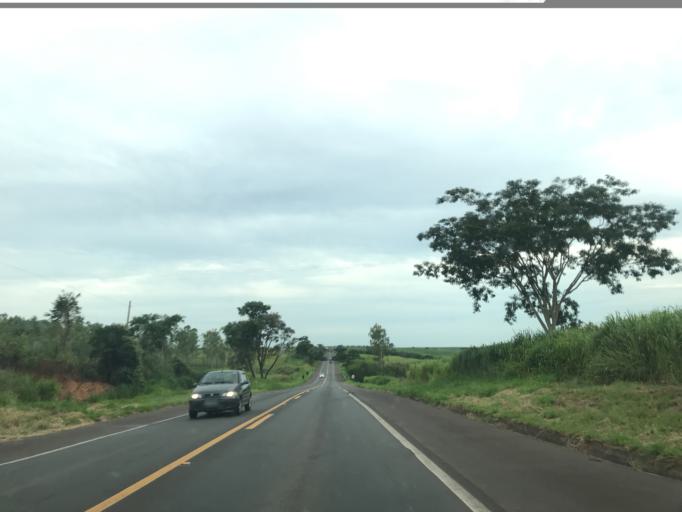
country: BR
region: Sao Paulo
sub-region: Birigui
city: Birigui
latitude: -21.5838
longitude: -50.4546
